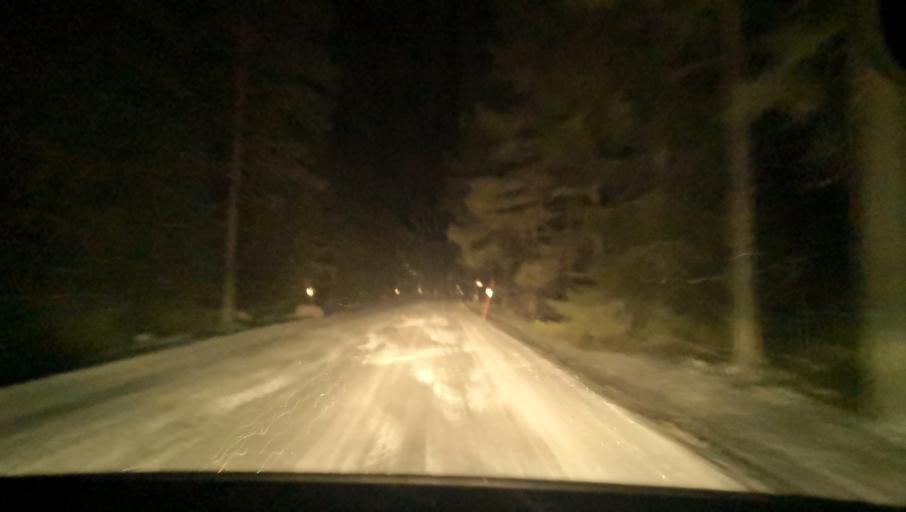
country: SE
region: Uppsala
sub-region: Heby Kommun
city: Tarnsjo
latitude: 60.1419
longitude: 16.9089
